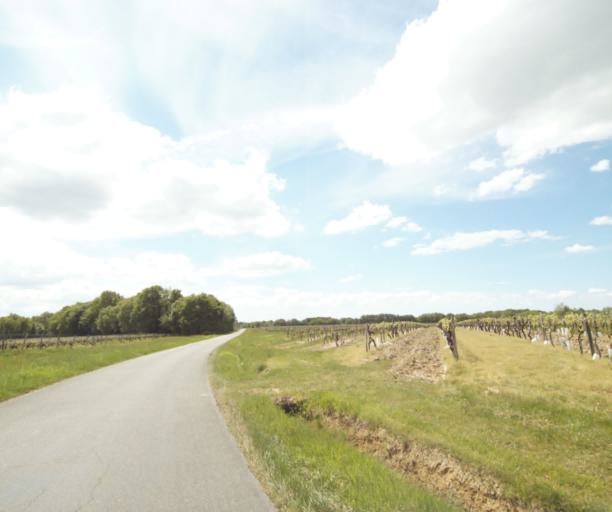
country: FR
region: Poitou-Charentes
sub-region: Departement de la Charente-Maritime
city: Burie
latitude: 45.7642
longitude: -0.4323
